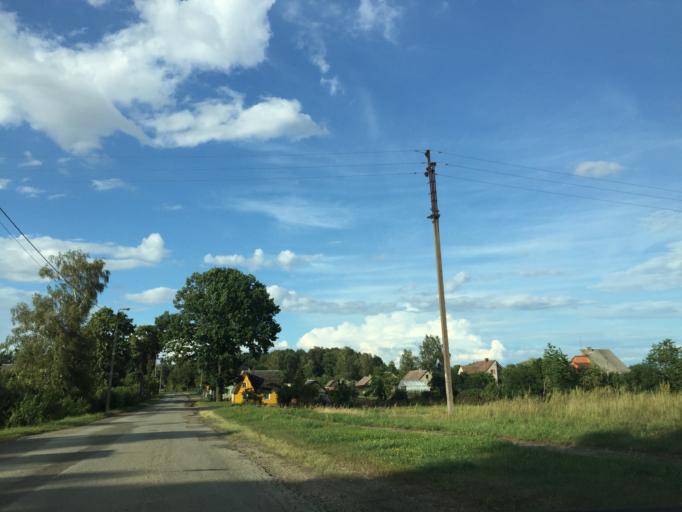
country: LT
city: Zagare
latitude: 56.3664
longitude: 23.2642
